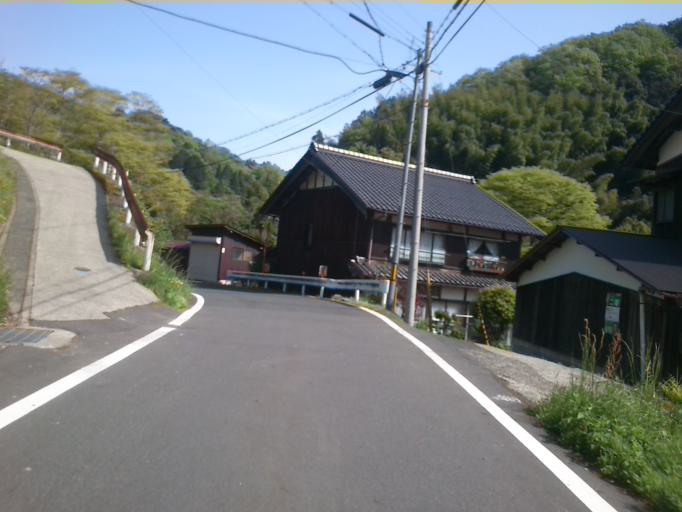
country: JP
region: Kyoto
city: Miyazu
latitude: 35.6329
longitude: 135.2312
